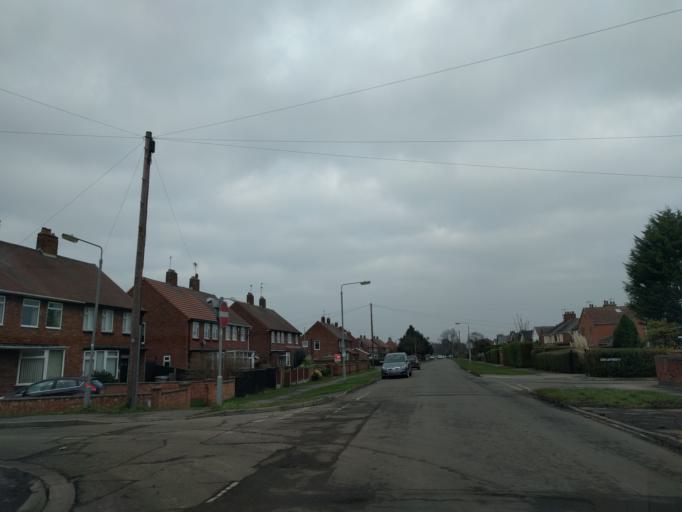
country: GB
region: England
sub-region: Nottinghamshire
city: Newark on Trent
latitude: 53.0877
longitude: -0.7990
